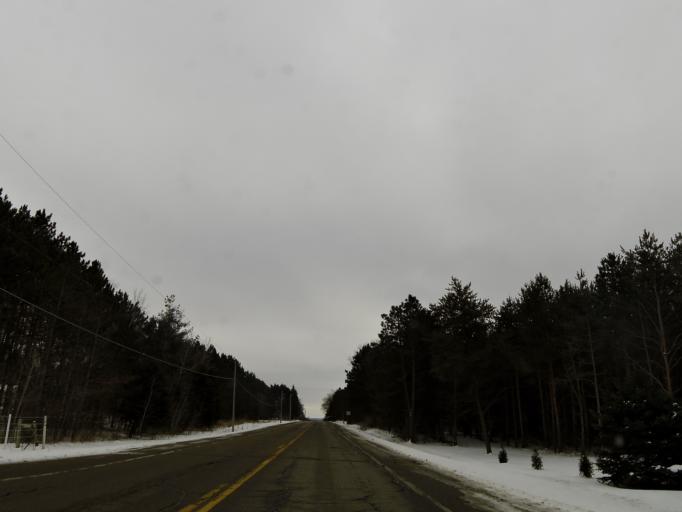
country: US
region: Minnesota
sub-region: Washington County
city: Oak Park Heights
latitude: 44.9844
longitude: -92.8224
